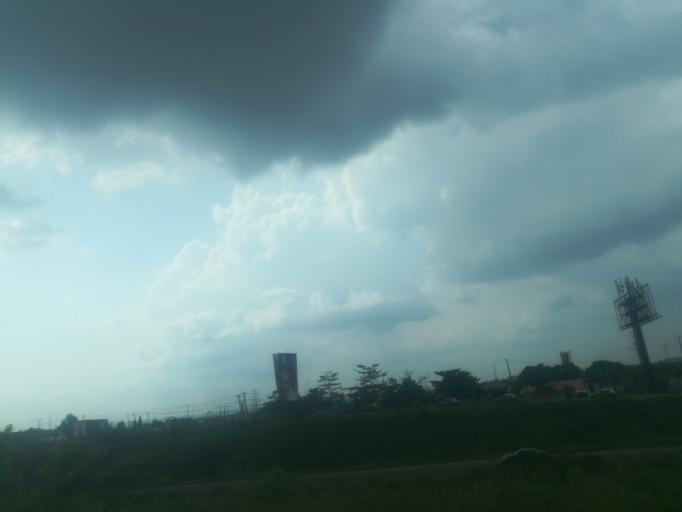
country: NG
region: Oyo
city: Ibadan
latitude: 7.3313
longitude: 3.8763
